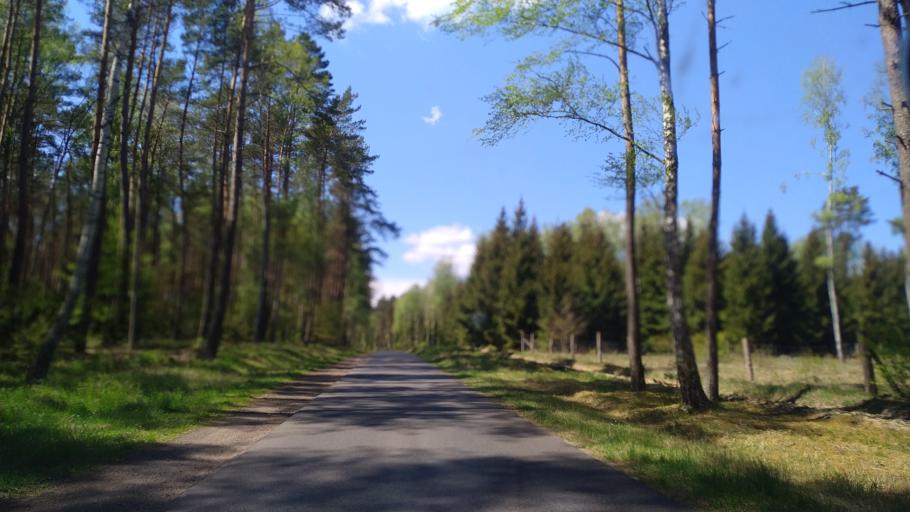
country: PL
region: Greater Poland Voivodeship
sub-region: Powiat zlotowski
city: Tarnowka
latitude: 53.2692
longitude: 16.8785
